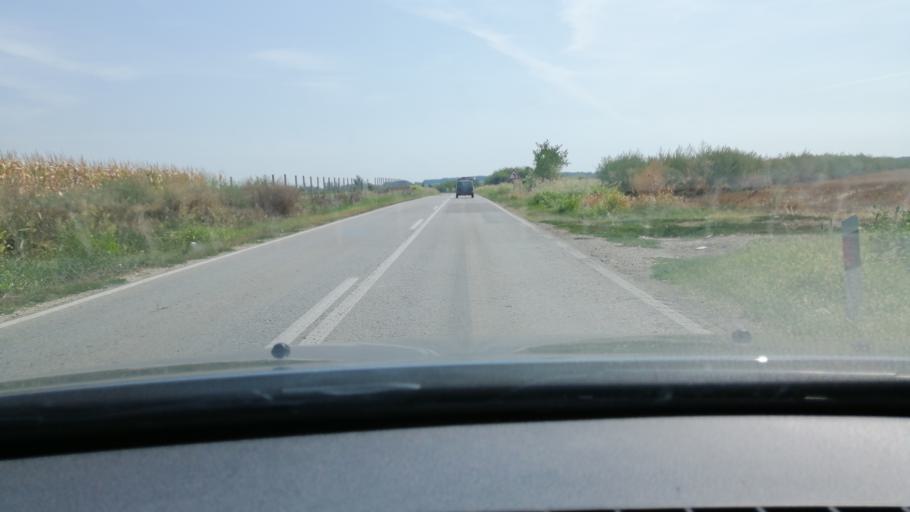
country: RS
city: Sutjeska
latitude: 45.3789
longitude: 20.7298
